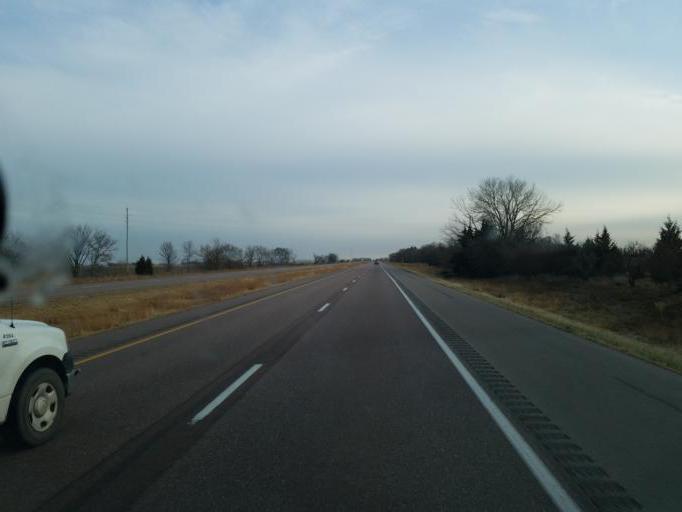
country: US
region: Iowa
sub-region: Monona County
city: Onawa
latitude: 42.1124
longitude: -96.1950
